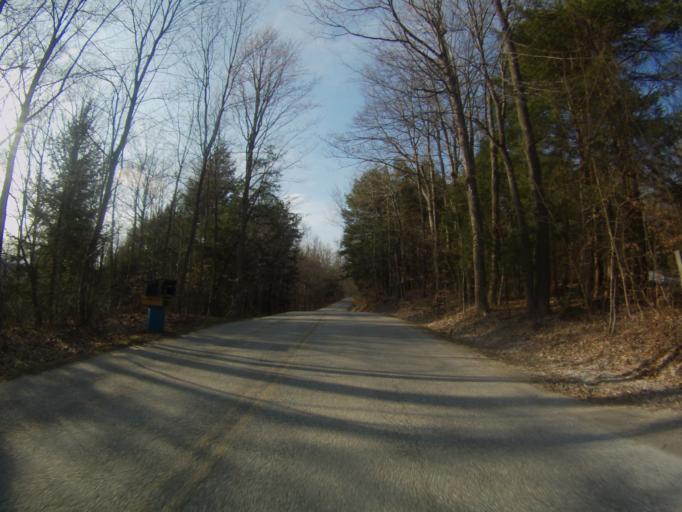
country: US
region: Vermont
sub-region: Addison County
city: Middlebury (village)
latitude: 44.0168
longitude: -73.2214
